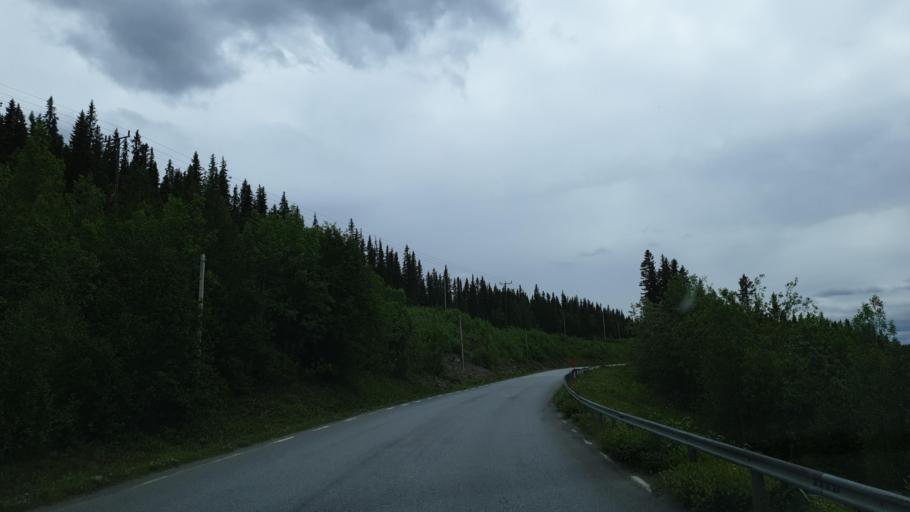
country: SE
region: Vaesterbotten
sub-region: Storumans Kommun
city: Fristad
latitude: 65.4227
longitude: 16.1712
